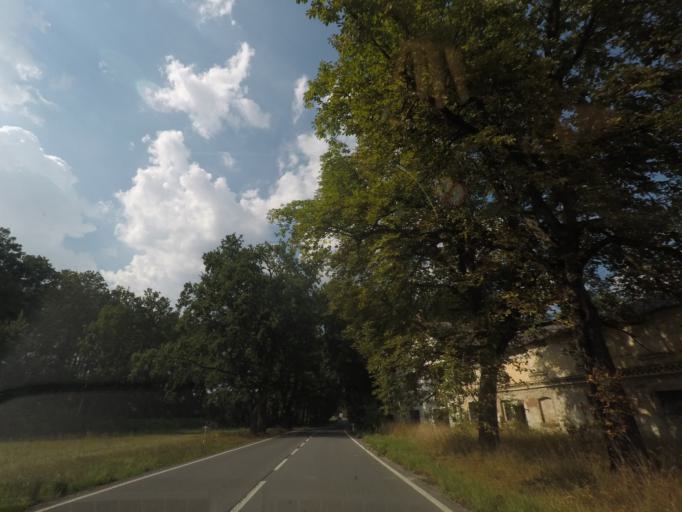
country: CZ
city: Albrechtice nad Orlici
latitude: 50.1281
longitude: 16.0647
